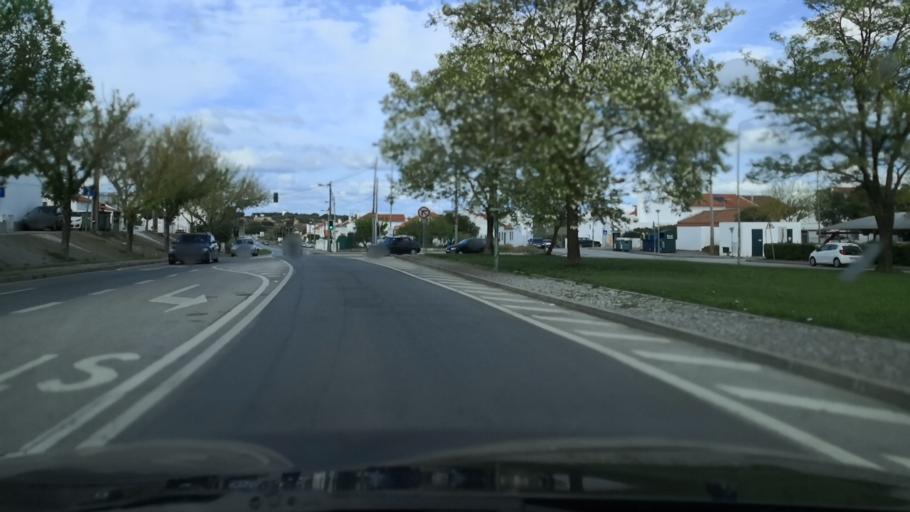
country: PT
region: Evora
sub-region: Evora
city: Evora
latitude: 38.5841
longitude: -7.8997
